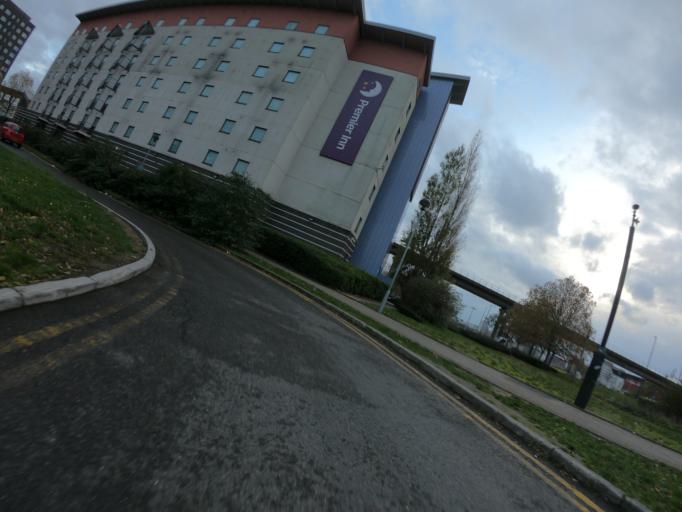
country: GB
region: England
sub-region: Greater London
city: East Ham
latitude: 51.5087
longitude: 0.0383
